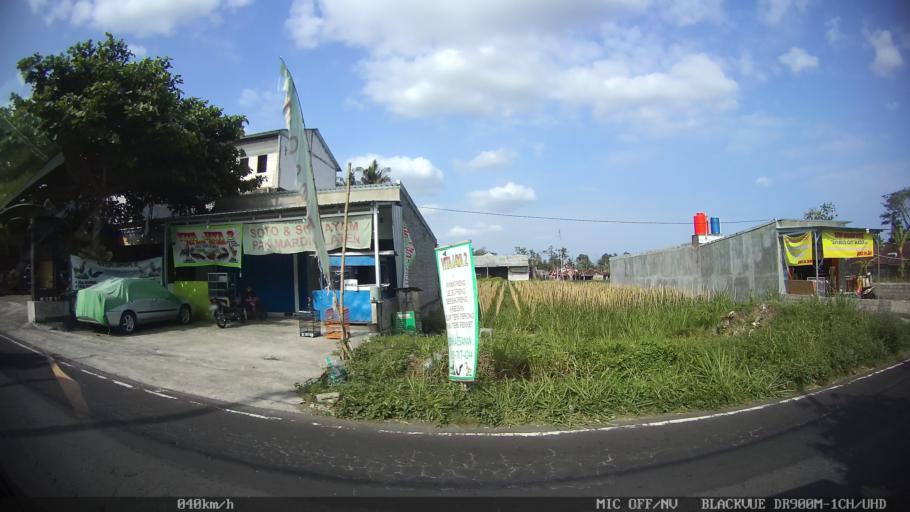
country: ID
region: Daerah Istimewa Yogyakarta
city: Depok
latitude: -7.7253
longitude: 110.4352
